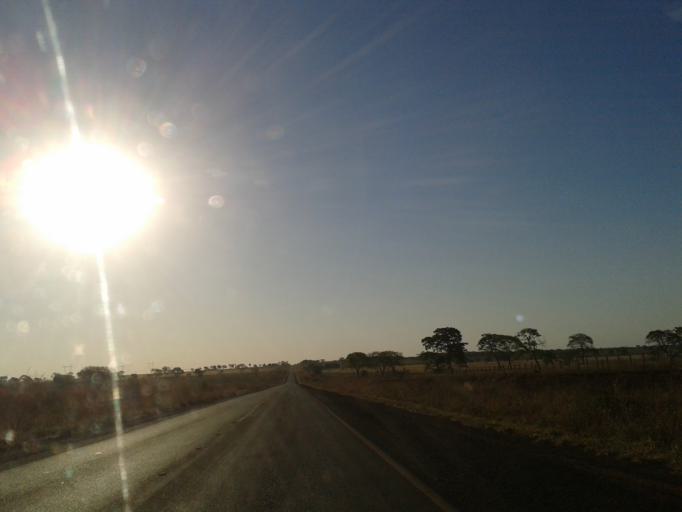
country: BR
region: Minas Gerais
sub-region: Santa Vitoria
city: Santa Vitoria
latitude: -19.1057
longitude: -50.3248
